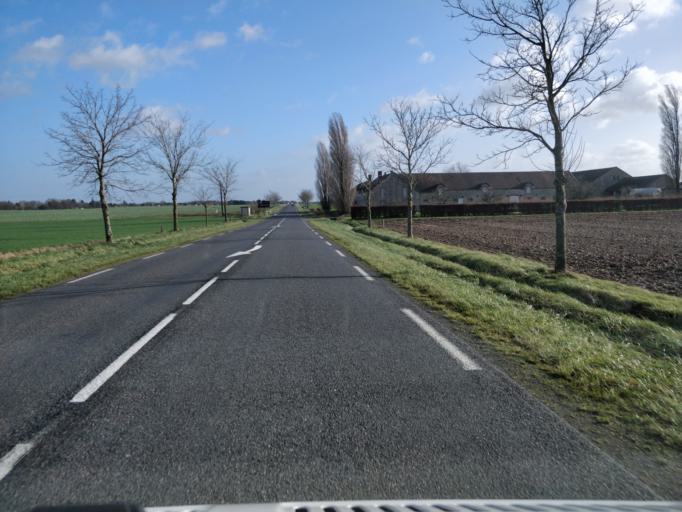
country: FR
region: Bourgogne
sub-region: Departement de l'Yonne
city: Cheroy
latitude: 48.2051
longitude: 2.9666
